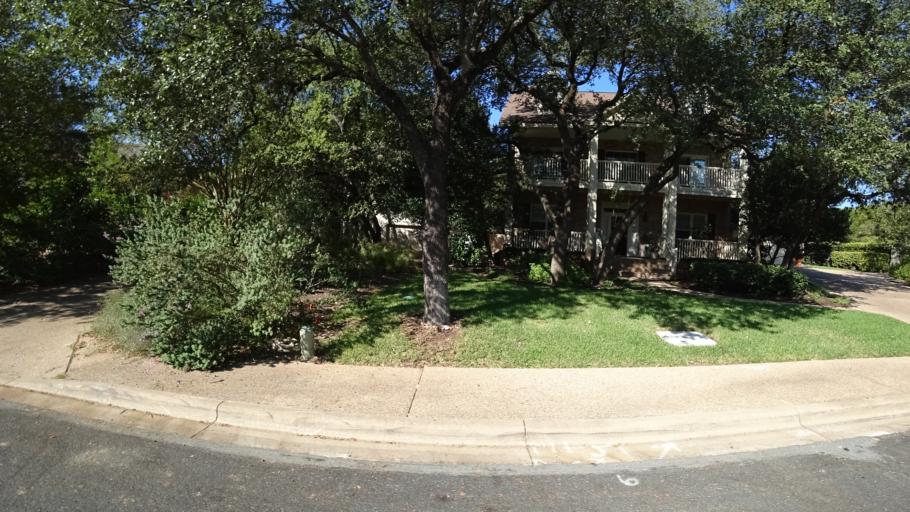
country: US
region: Texas
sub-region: Travis County
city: Rollingwood
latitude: 30.2632
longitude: -97.8099
